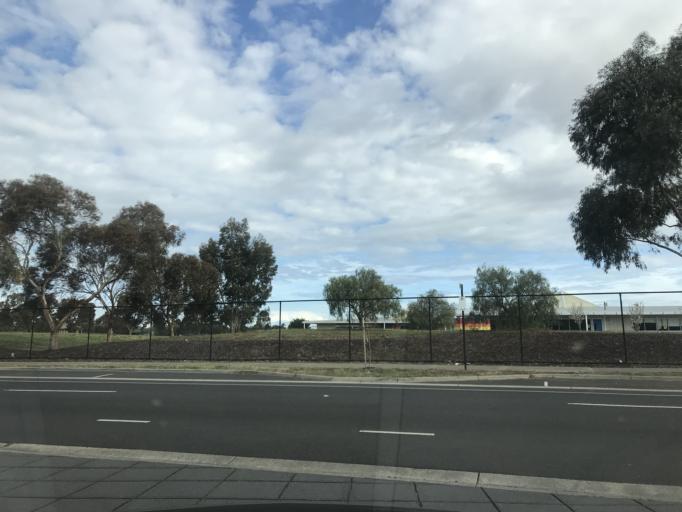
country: AU
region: Victoria
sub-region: Wyndham
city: Williams Landing
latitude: -37.8864
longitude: 144.7344
